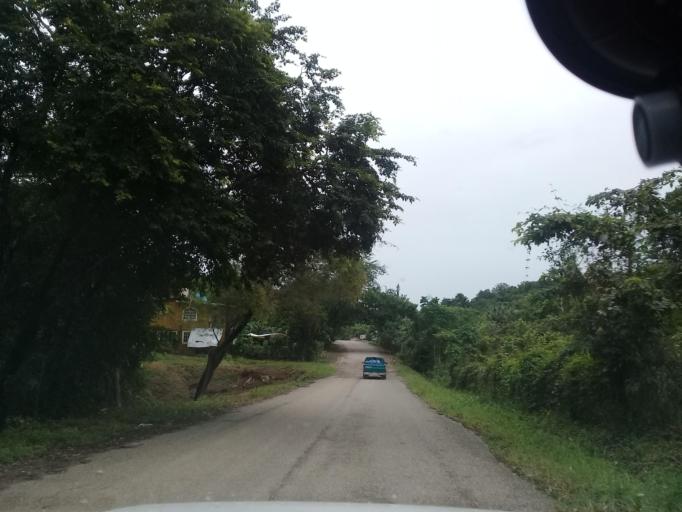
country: MX
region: Veracruz
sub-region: Chalma
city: San Pedro Coyutla
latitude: 21.2150
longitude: -98.3740
